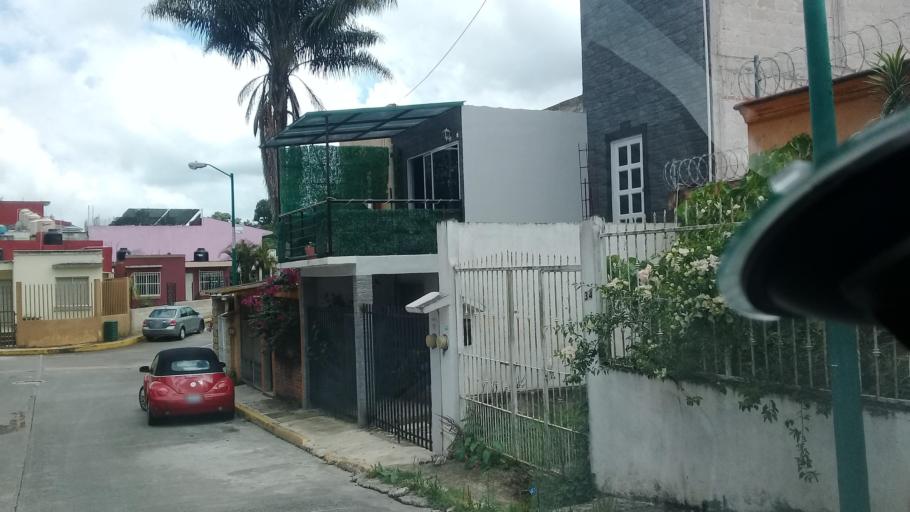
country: MX
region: Veracruz
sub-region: Xalapa
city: Lomas Verdes
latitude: 19.5025
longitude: -96.8913
